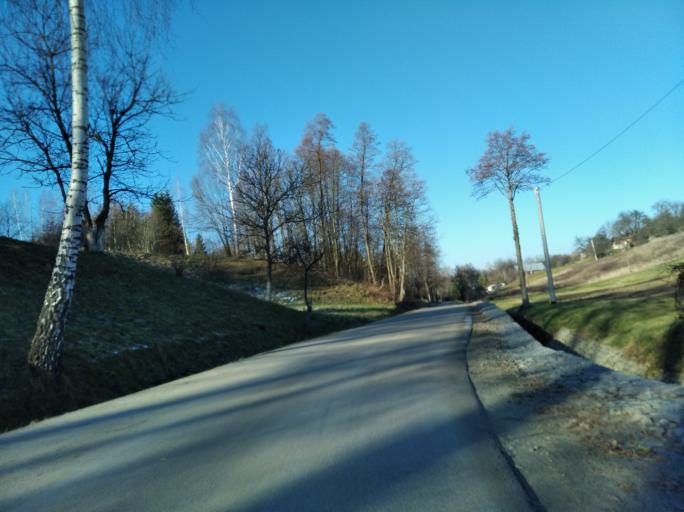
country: PL
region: Subcarpathian Voivodeship
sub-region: Powiat strzyzowski
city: Wysoka Strzyzowska
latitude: 49.8446
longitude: 21.7657
